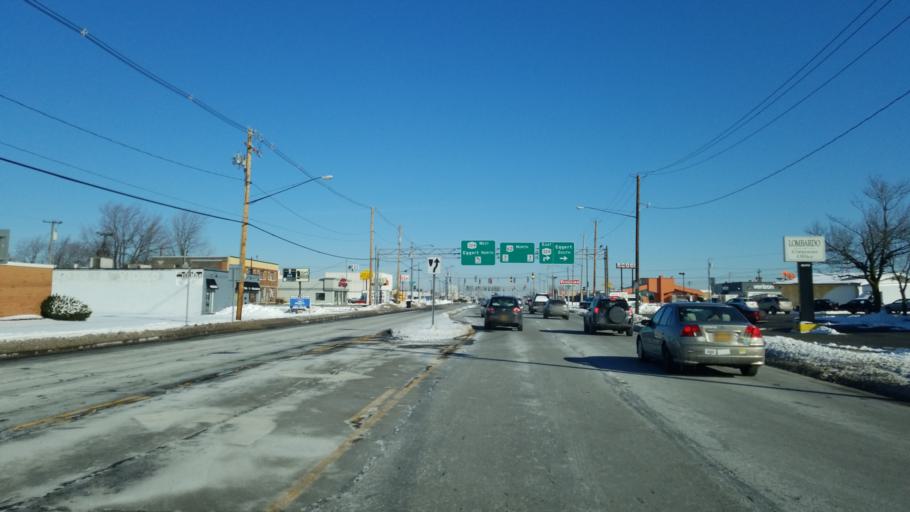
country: US
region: New York
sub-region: Erie County
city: Amherst
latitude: 42.9783
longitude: -78.8230
